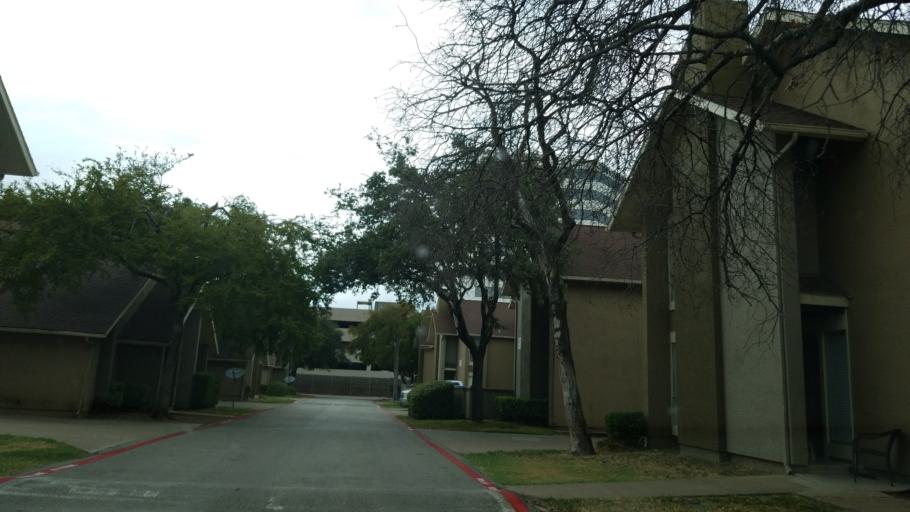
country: US
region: Texas
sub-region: Dallas County
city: Richardson
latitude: 32.9485
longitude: -96.7705
